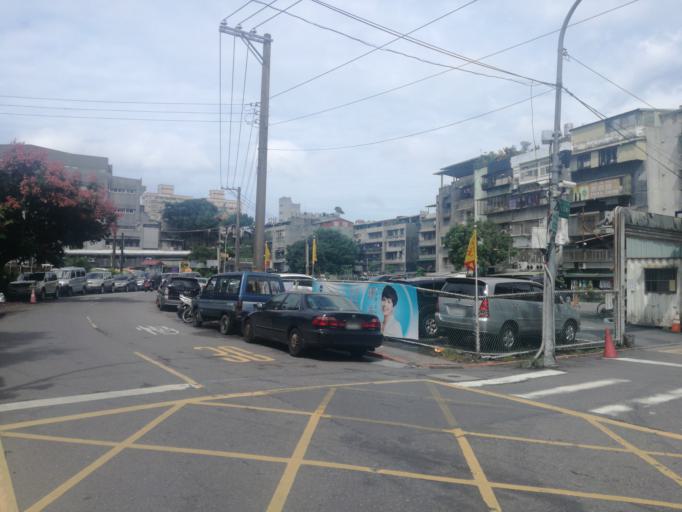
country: TW
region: Taipei
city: Taipei
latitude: 24.9981
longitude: 121.5569
